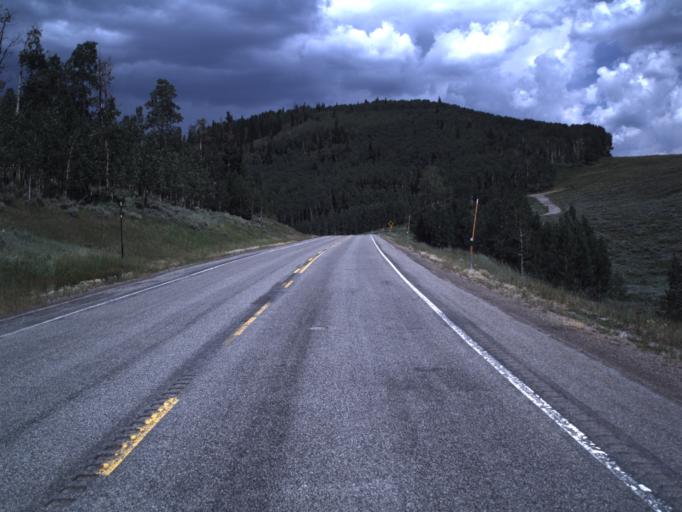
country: US
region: Utah
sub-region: Sanpete County
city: Fairview
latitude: 39.5865
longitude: -111.2283
